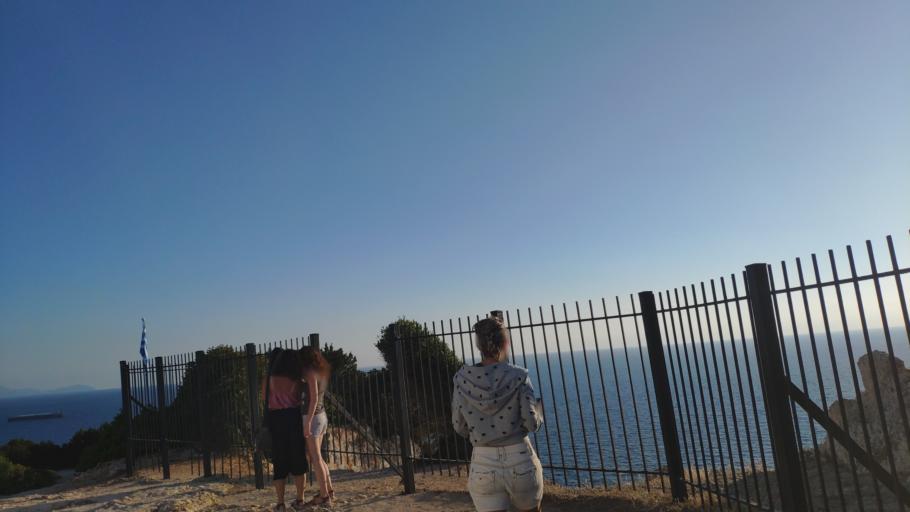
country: GR
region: Ionian Islands
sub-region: Lefkada
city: Nidri
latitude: 38.5636
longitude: 20.5425
